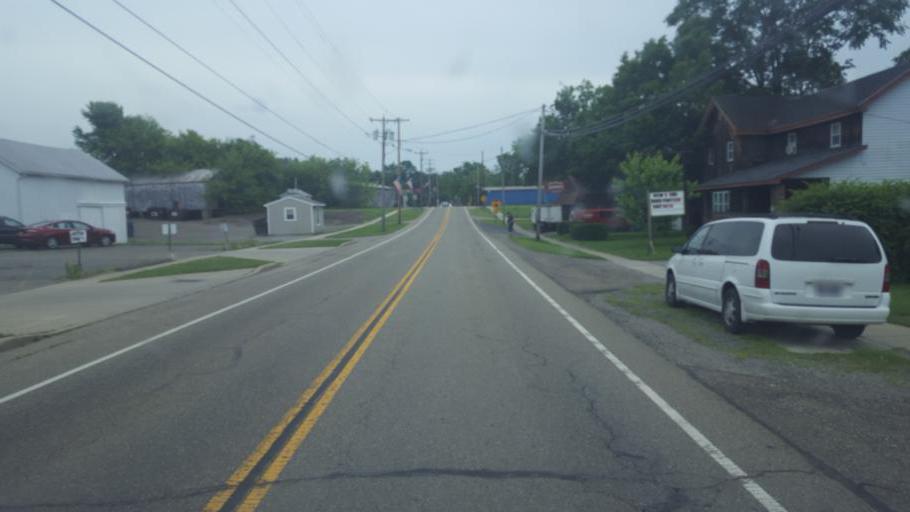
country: US
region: Ohio
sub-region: Trumbull County
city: Cortland
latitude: 41.3318
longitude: -80.7313
